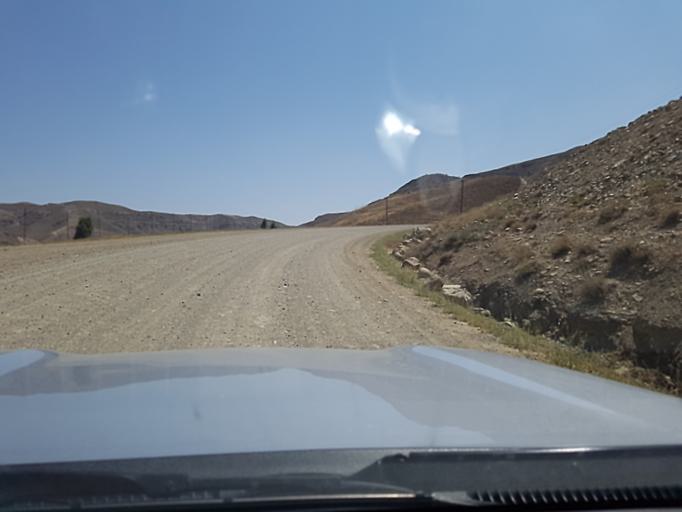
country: TM
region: Balkan
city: Magtymguly
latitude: 38.3439
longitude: 56.7380
